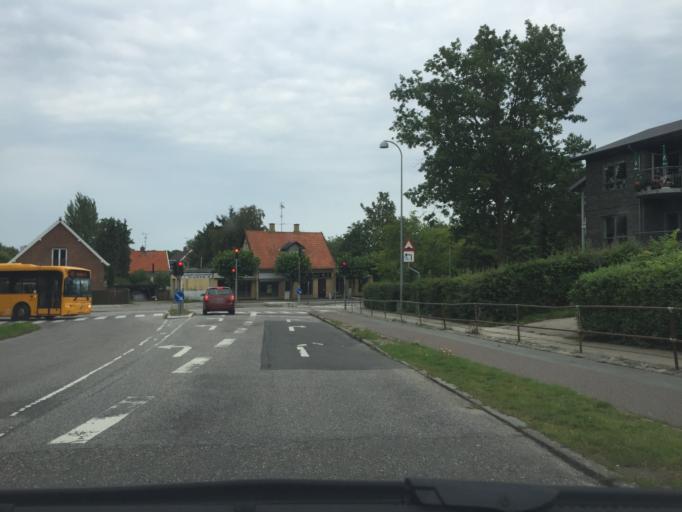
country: DK
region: Capital Region
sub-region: Lyngby-Tarbaek Kommune
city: Kongens Lyngby
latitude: 55.7964
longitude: 12.5234
